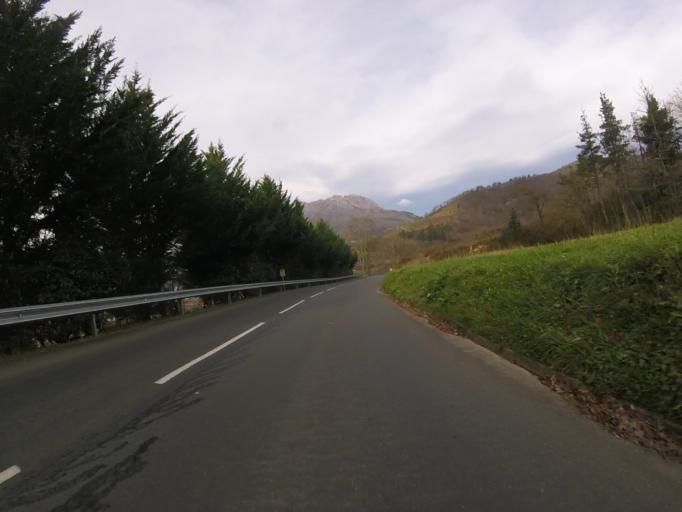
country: ES
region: Basque Country
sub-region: Provincia de Guipuzcoa
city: Azpeitia
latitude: 43.1735
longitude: -2.2476
